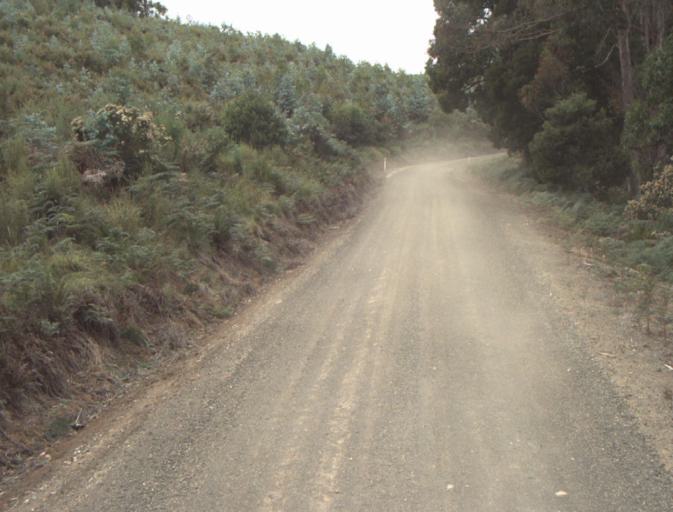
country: AU
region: Tasmania
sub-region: Northern Midlands
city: Evandale
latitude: -41.4554
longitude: 147.4725
